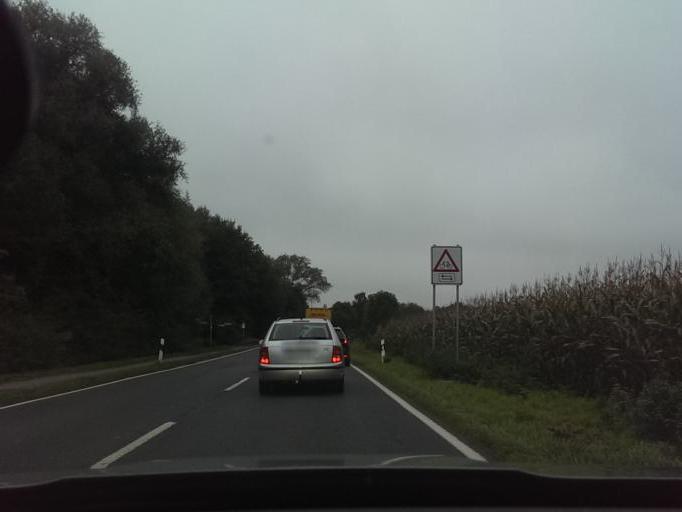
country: DE
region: Lower Saxony
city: Garbsen
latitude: 52.4052
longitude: 9.5926
